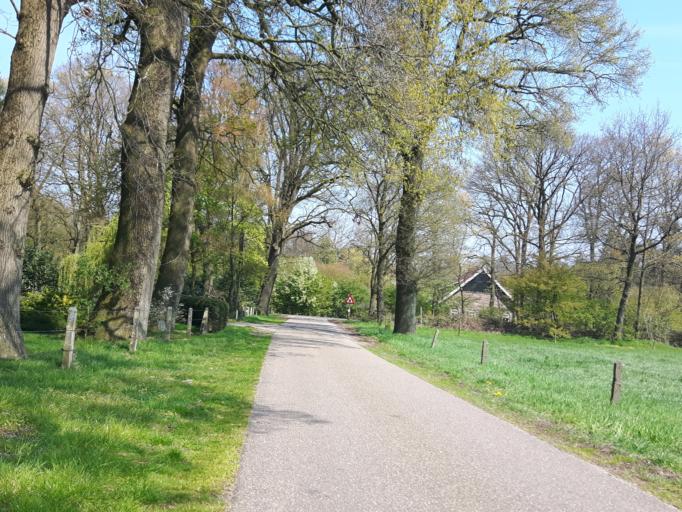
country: NL
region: Overijssel
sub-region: Gemeente Haaksbergen
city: Haaksbergen
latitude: 52.1497
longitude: 6.8204
